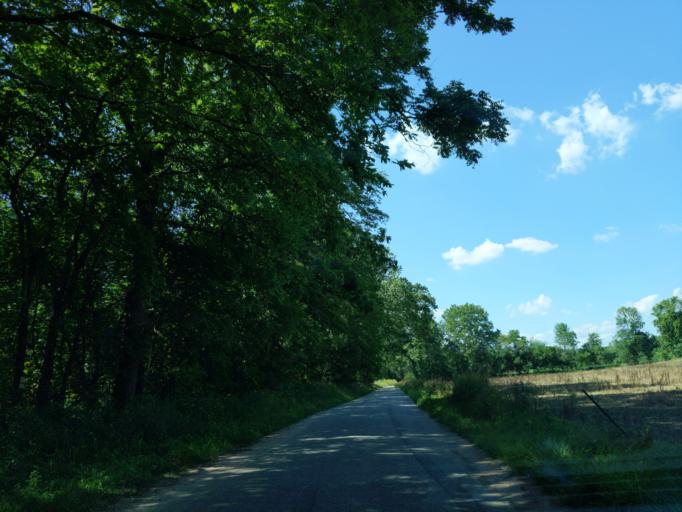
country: US
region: Indiana
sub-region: Ripley County
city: Osgood
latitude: 39.2025
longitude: -85.4157
